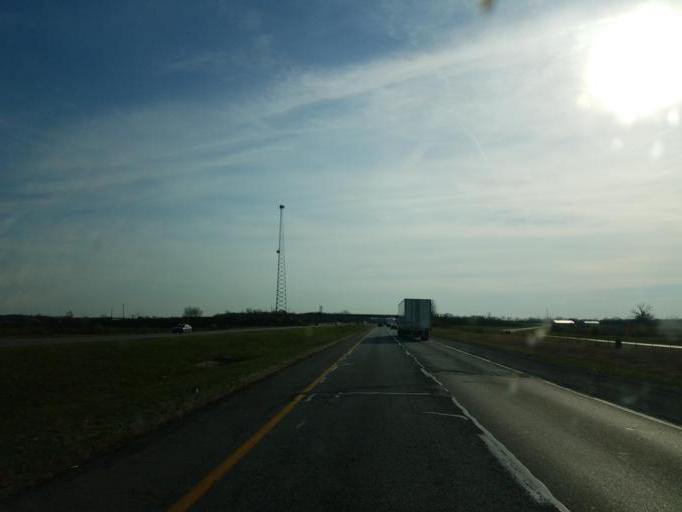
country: US
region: Ohio
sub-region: Madison County
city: Mount Sterling
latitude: 39.7716
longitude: -83.2753
